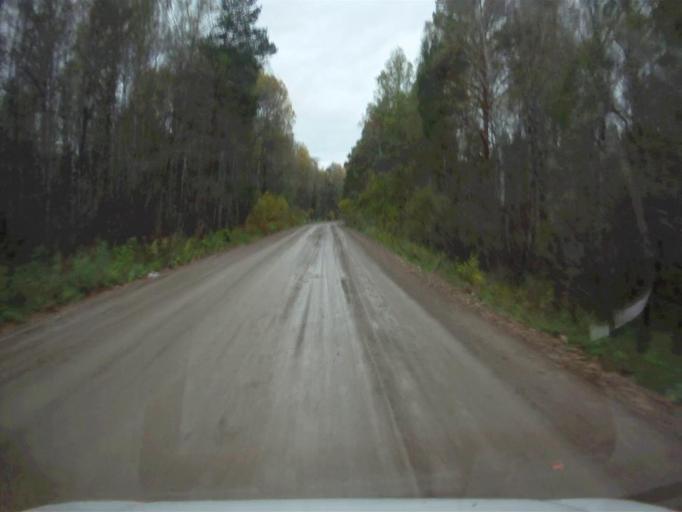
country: RU
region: Chelyabinsk
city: Nyazepetrovsk
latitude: 56.1267
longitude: 59.3380
